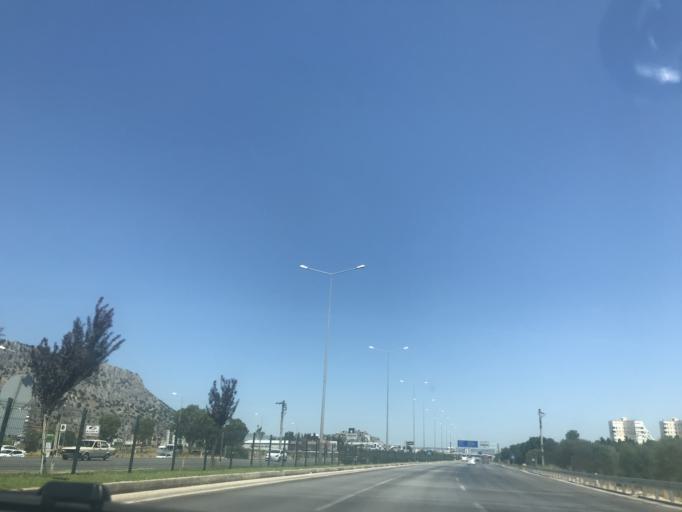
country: TR
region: Antalya
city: Cakirlar
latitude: 36.8395
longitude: 30.5965
